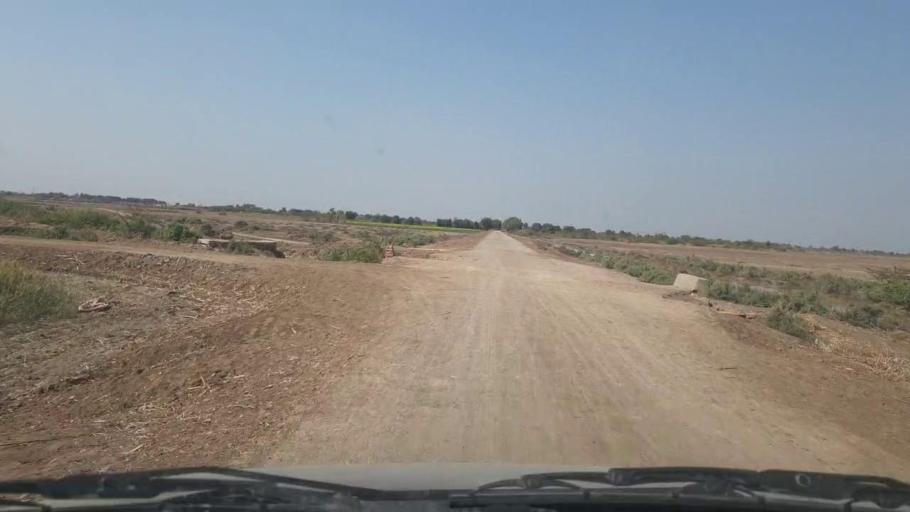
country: PK
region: Sindh
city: Samaro
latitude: 25.2350
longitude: 69.3333
